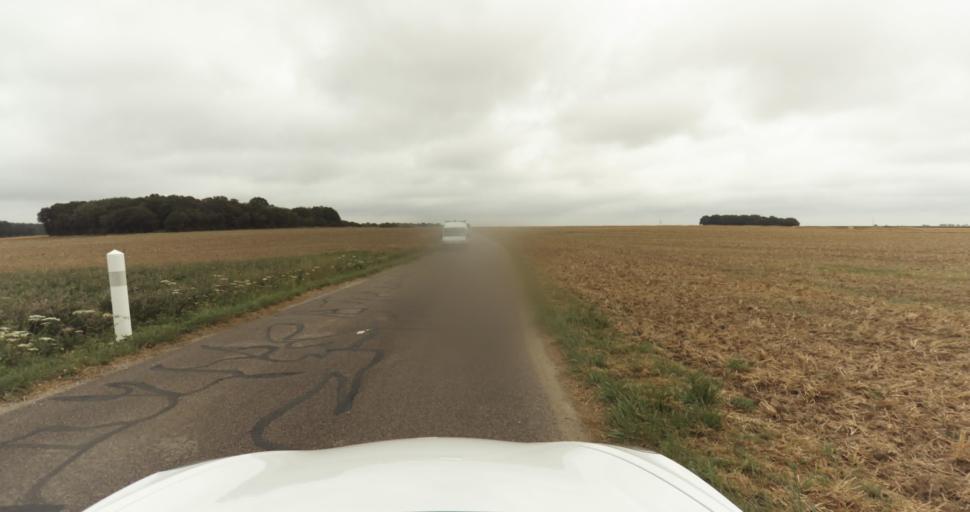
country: FR
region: Haute-Normandie
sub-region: Departement de l'Eure
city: Aviron
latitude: 49.0697
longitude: 1.1046
